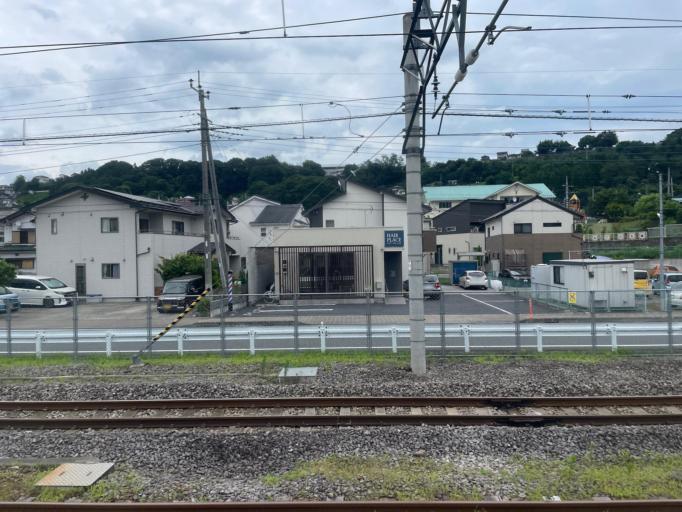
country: JP
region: Gunma
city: Numata
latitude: 36.6408
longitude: 139.0368
